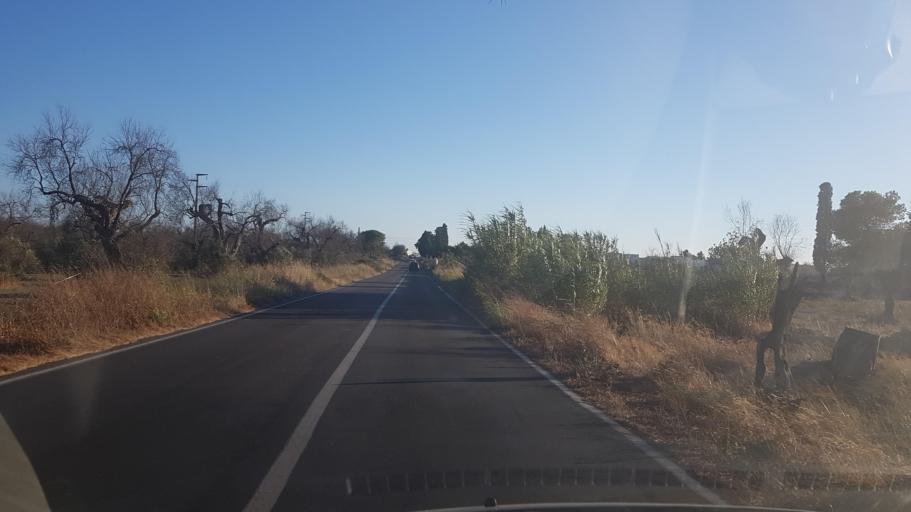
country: IT
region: Apulia
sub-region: Provincia di Lecce
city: Struda
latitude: 40.3291
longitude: 18.2905
